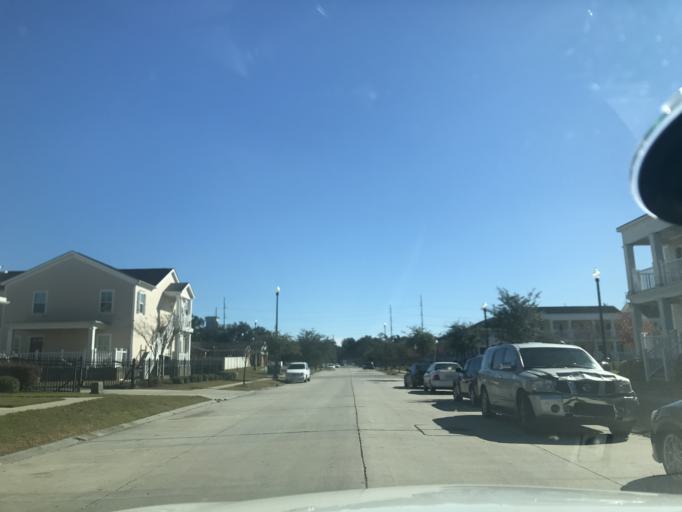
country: US
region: Louisiana
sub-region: Orleans Parish
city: New Orleans
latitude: 29.9518
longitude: -90.0946
